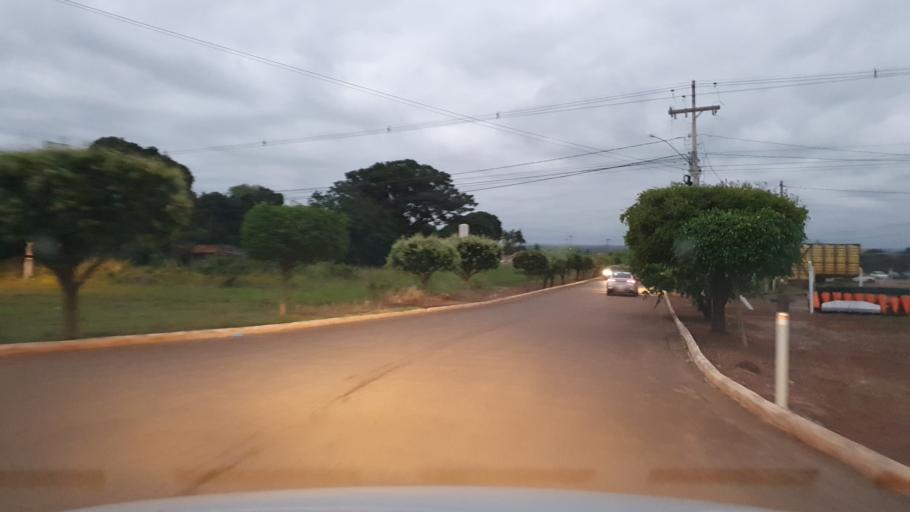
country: BR
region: Mato Grosso
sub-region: Pontes E Lacerda
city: Pontes e Lacerda
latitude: -15.2335
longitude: -59.3175
